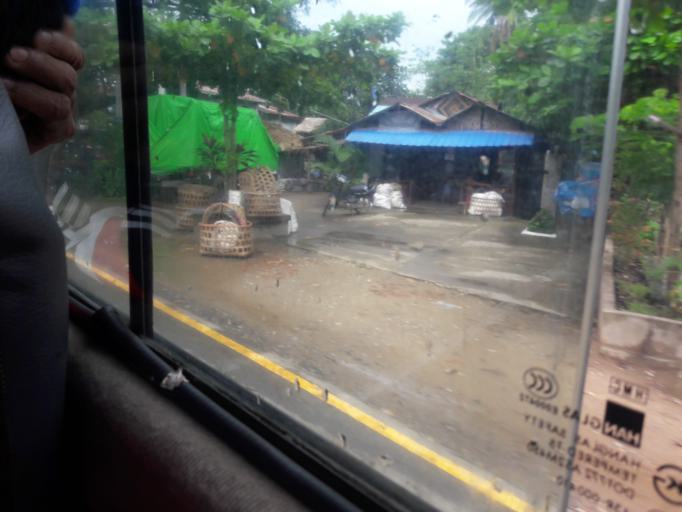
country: MM
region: Bago
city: Nyaunglebin
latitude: 17.7735
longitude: 96.6436
